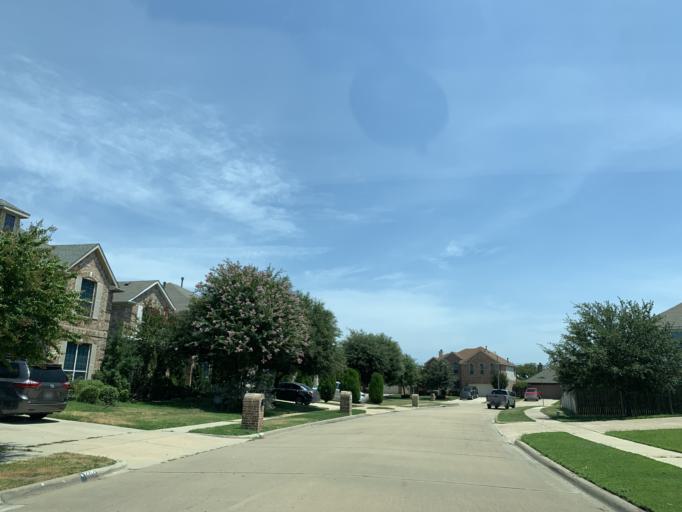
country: US
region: Texas
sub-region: Dallas County
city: Grand Prairie
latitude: 32.6517
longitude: -97.0364
